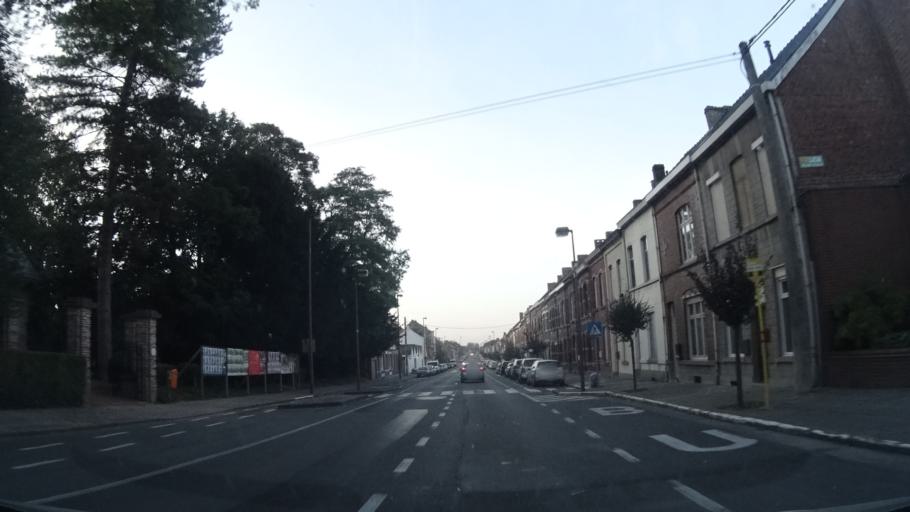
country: BE
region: Wallonia
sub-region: Province du Hainaut
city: Frasnes-lez-Buissenal
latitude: 50.5944
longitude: 3.6173
